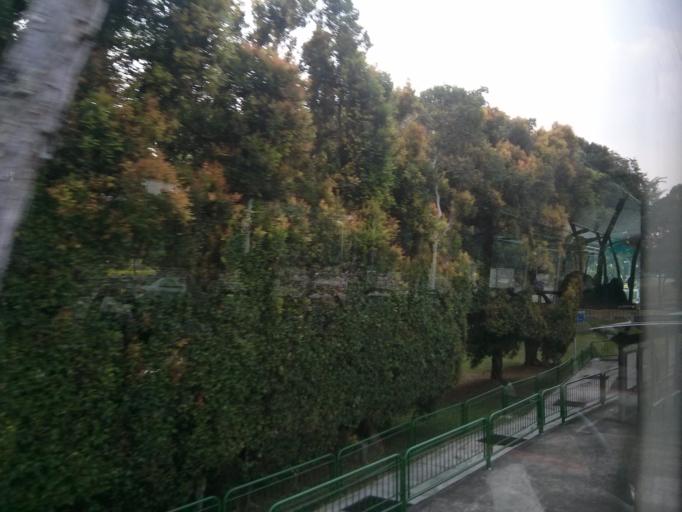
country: SG
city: Singapore
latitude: 1.3453
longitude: 103.8382
